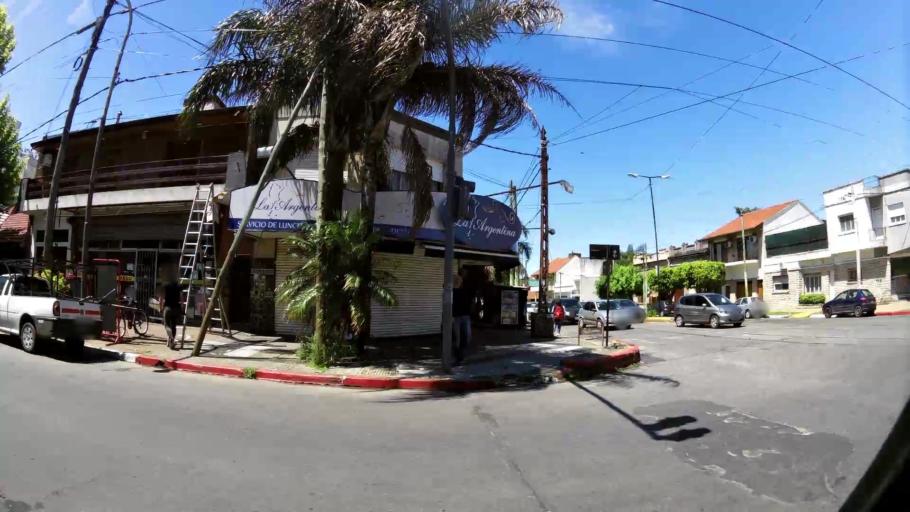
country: AR
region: Buenos Aires
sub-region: Partido de Quilmes
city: Quilmes
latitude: -34.7133
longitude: -58.2779
